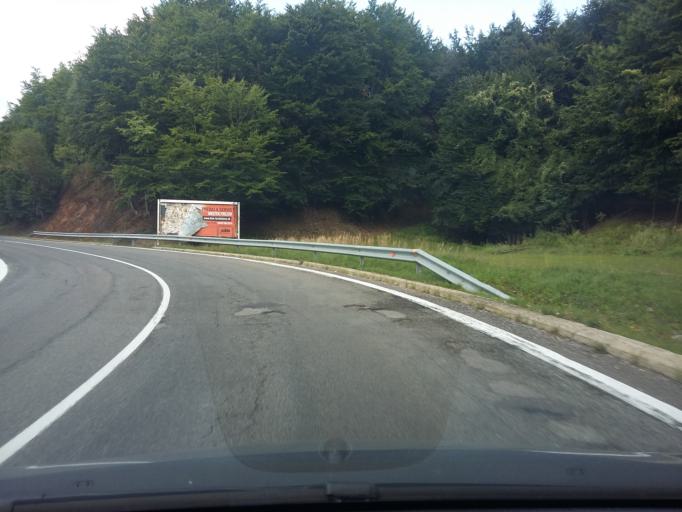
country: SK
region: Bratislavsky
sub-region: Okres Pezinok
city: Pezinok
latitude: 48.3516
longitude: 17.2161
